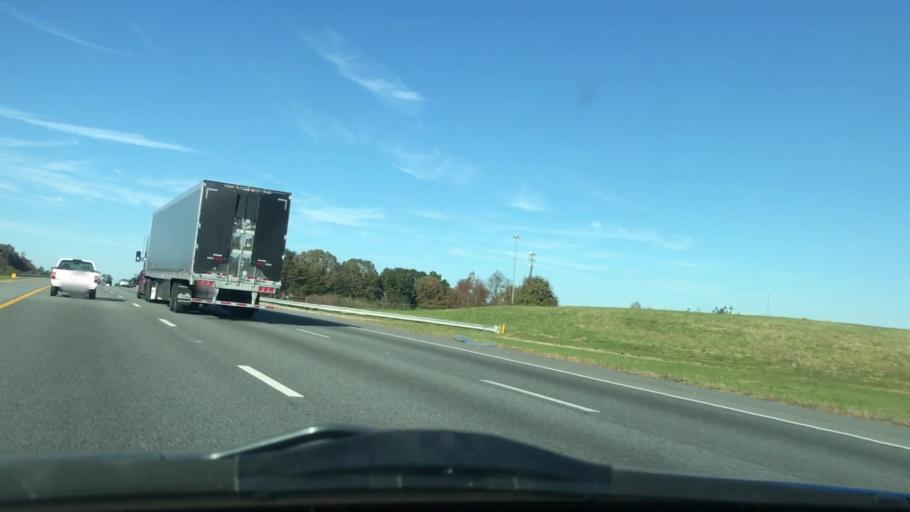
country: US
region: North Carolina
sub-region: Guilford County
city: High Point
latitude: 35.9647
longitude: -79.9747
